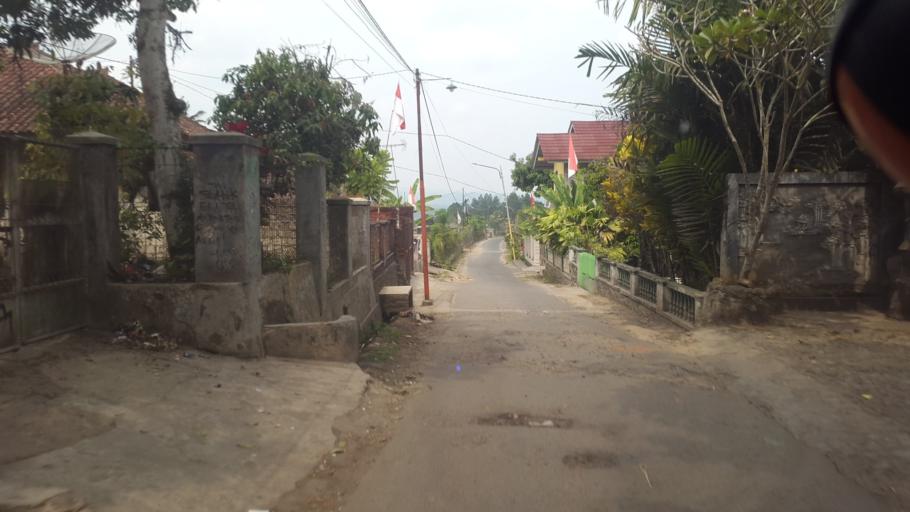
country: ID
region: West Java
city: Cicurug
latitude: -6.7688
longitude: 106.7689
